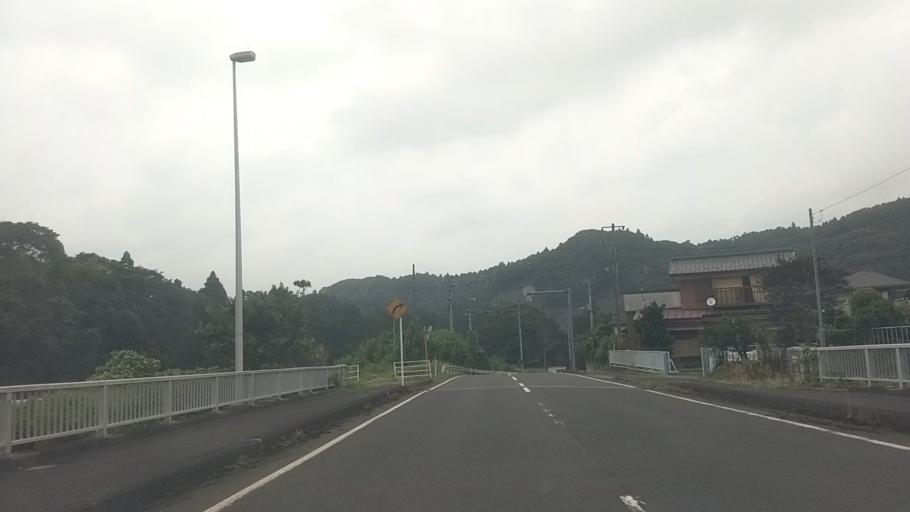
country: JP
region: Chiba
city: Ohara
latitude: 35.2678
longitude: 140.2540
